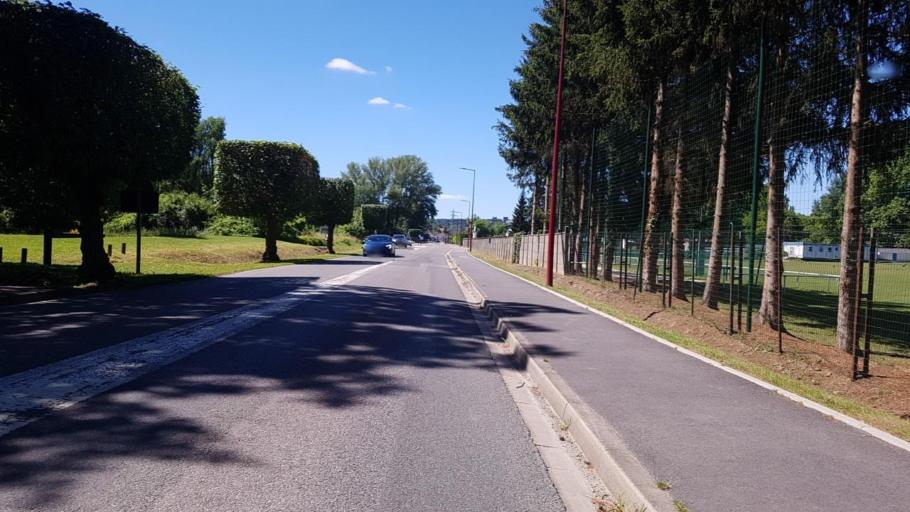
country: FR
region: Ile-de-France
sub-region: Departement de Seine-et-Marne
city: La Ferte-sous-Jouarre
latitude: 48.9569
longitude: 3.1419
